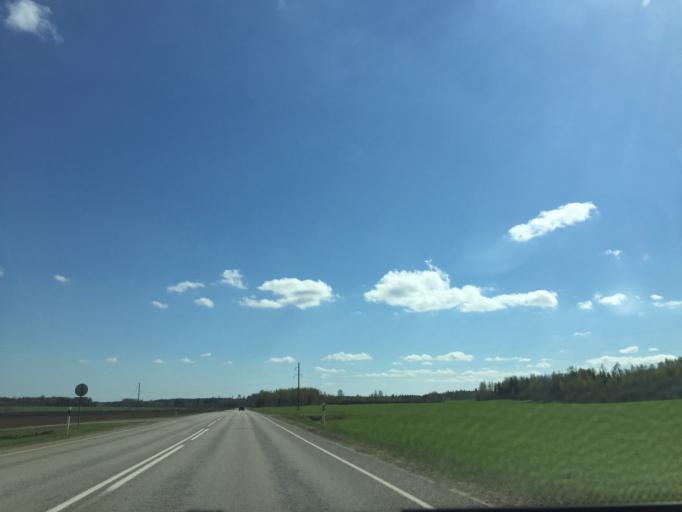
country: EE
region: Valgamaa
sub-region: Valga linn
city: Valga
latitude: 57.8826
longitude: 26.0592
